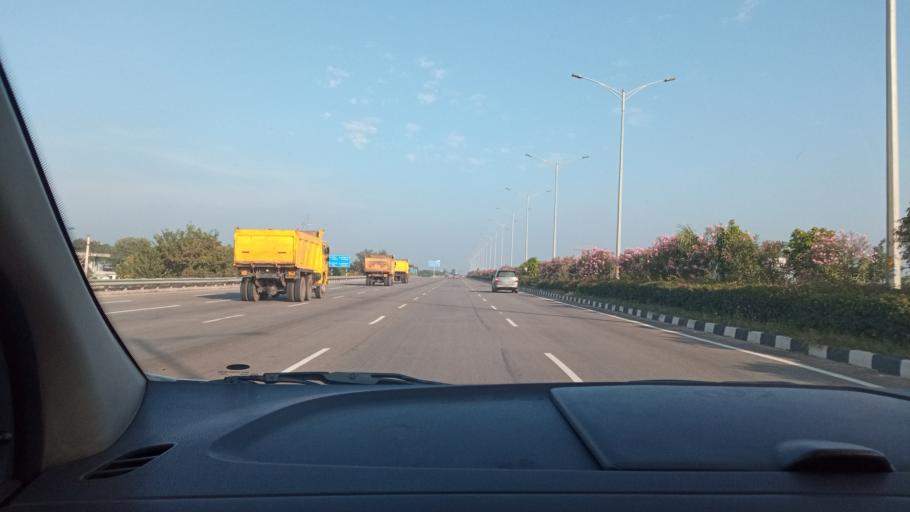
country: IN
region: Telangana
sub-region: Hyderabad
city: Hyderabad
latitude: 17.3427
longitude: 78.3640
